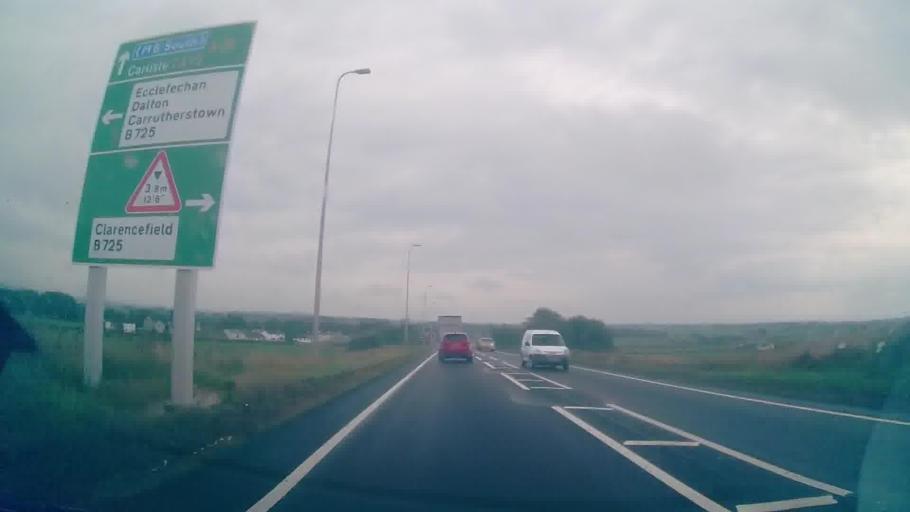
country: GB
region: Scotland
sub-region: Dumfries and Galloway
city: Lochmaben
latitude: 55.0335
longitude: -3.4117
